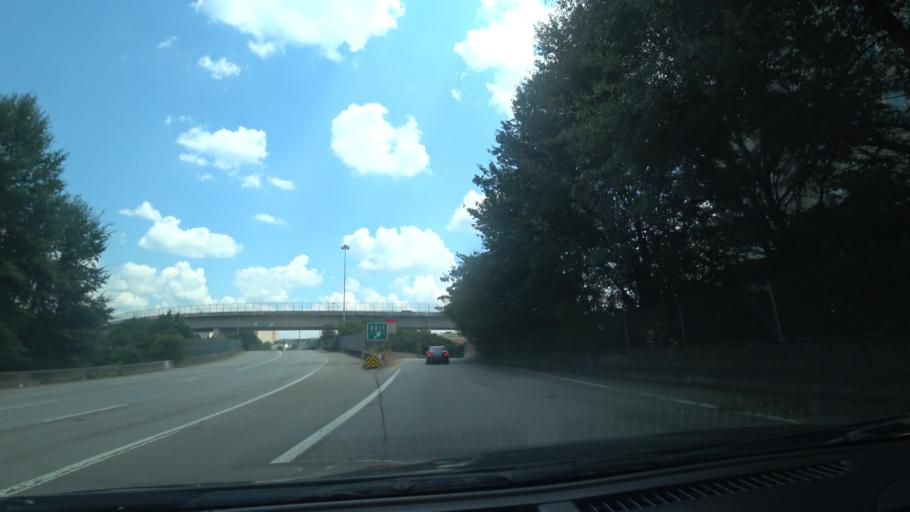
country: US
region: Georgia
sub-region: Fulton County
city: Atlanta
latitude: 33.7583
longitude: -84.3810
